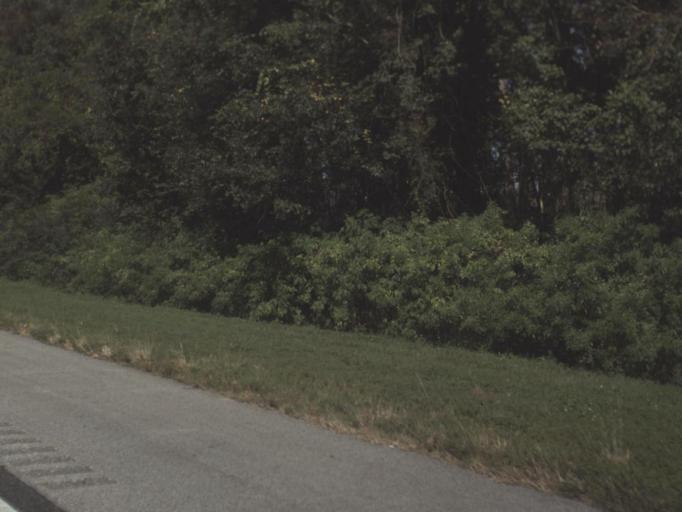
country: US
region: Florida
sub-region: Sumter County
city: Wildwood
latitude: 28.8495
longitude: -82.0822
